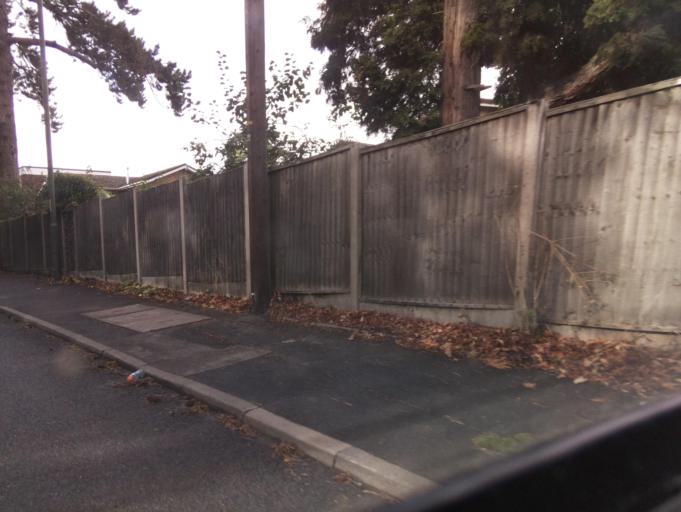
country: GB
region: England
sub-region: Worcestershire
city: Kidderminster
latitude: 52.3828
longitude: -2.2300
